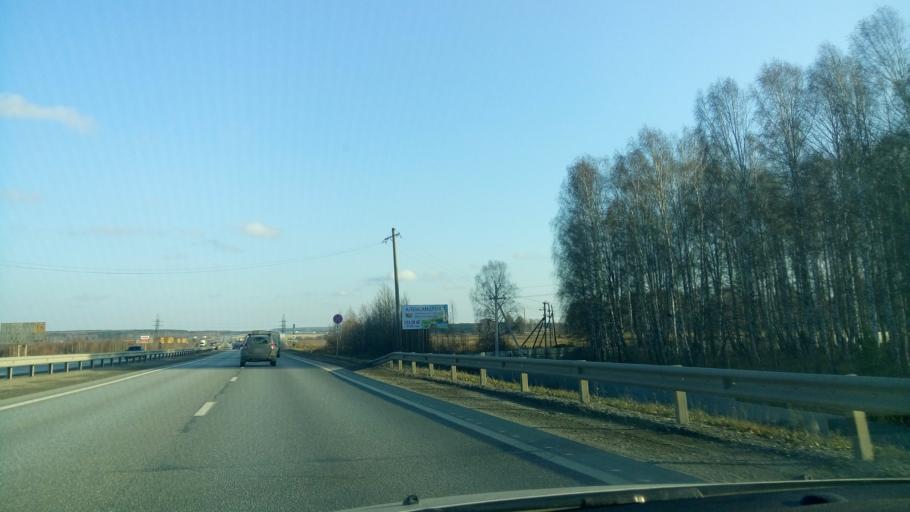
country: RU
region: Sverdlovsk
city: Bobrovskiy
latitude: 56.7585
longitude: 60.9298
